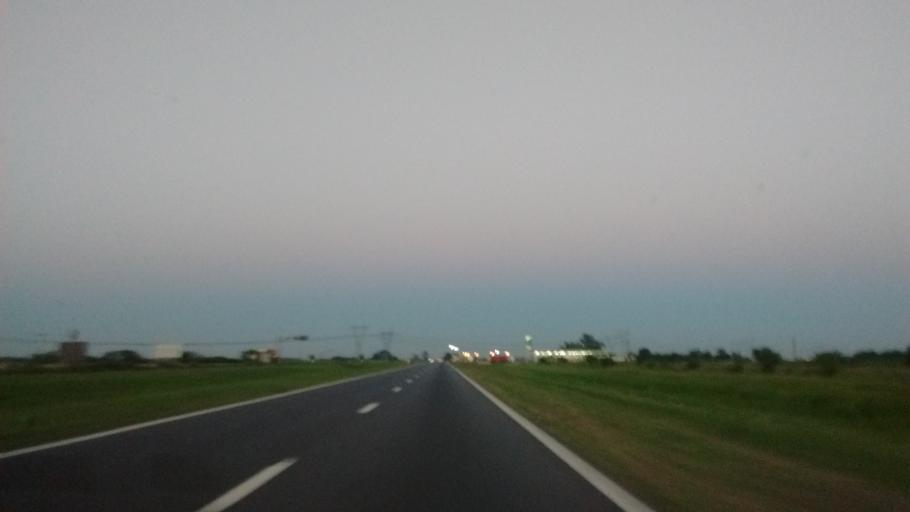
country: AR
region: Santa Fe
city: Roldan
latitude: -32.9255
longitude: -60.9067
